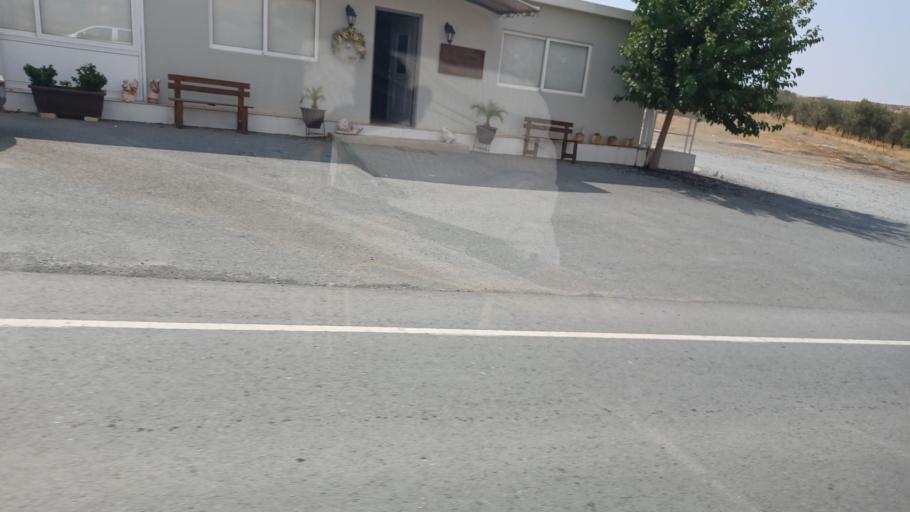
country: CY
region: Larnaka
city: Aradippou
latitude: 34.9410
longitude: 33.5555
